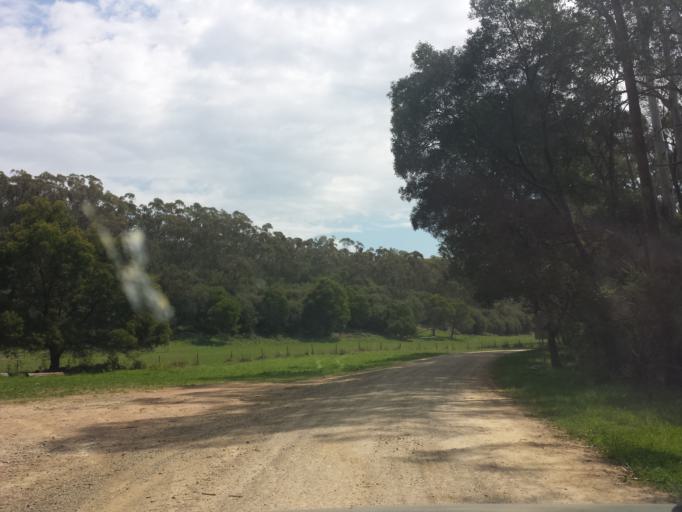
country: AU
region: Victoria
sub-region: Murrindindi
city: Alexandra
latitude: -37.3428
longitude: 145.7486
